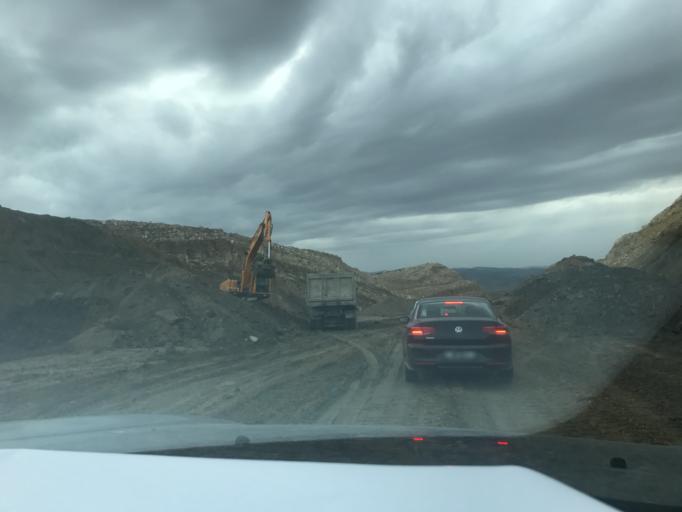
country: TN
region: Silyanah
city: Siliana
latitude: 36.0884
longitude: 9.4604
